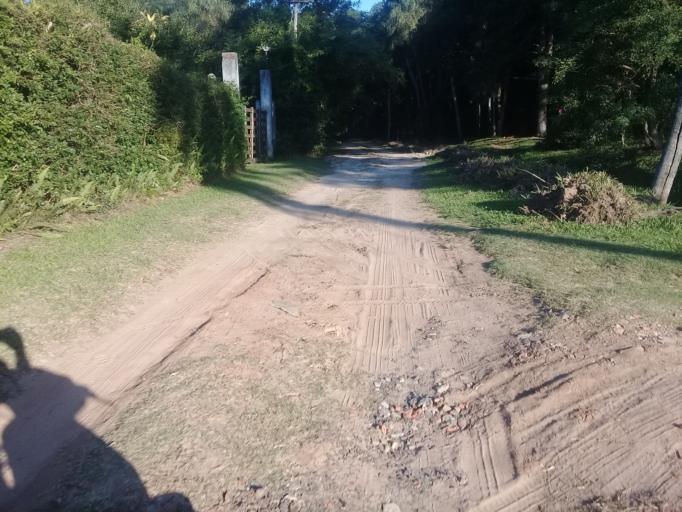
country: AR
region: Corrientes
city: San Luis del Palmar
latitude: -27.4608
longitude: -58.6644
